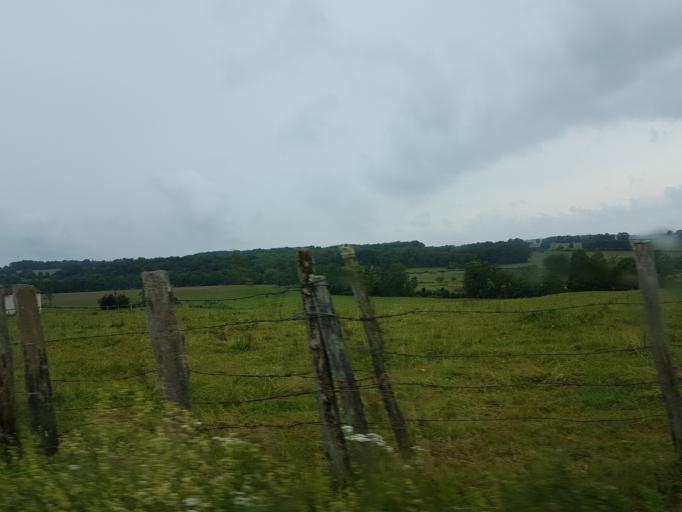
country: FR
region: Bourgogne
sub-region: Departement de la Nievre
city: Corbigny
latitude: 47.2013
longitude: 3.7219
